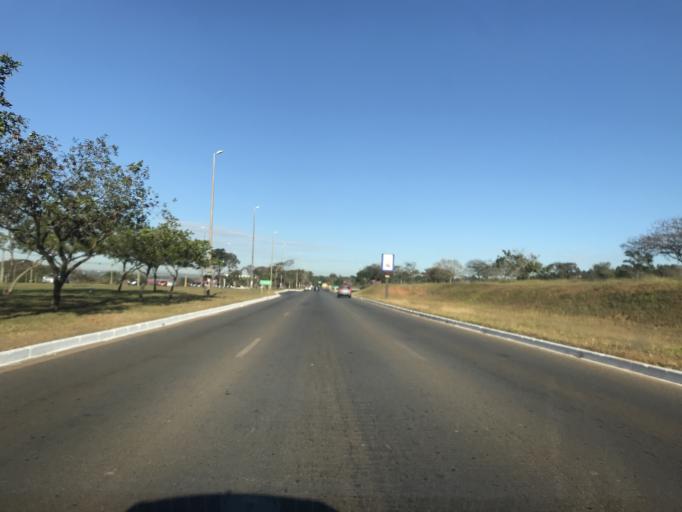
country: BR
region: Federal District
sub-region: Brasilia
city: Brasilia
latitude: -15.8174
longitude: -47.8763
